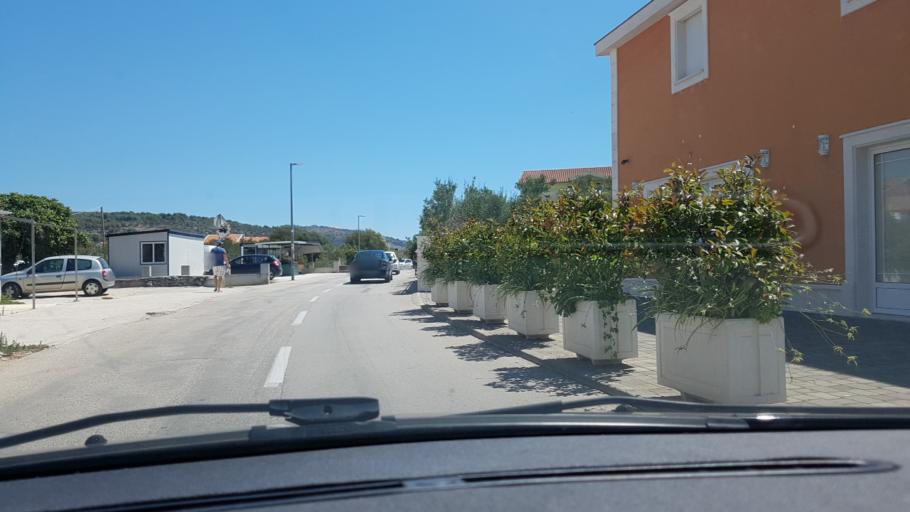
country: HR
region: Splitsko-Dalmatinska
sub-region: Grad Trogir
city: Trogir
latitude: 43.4923
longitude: 16.2655
